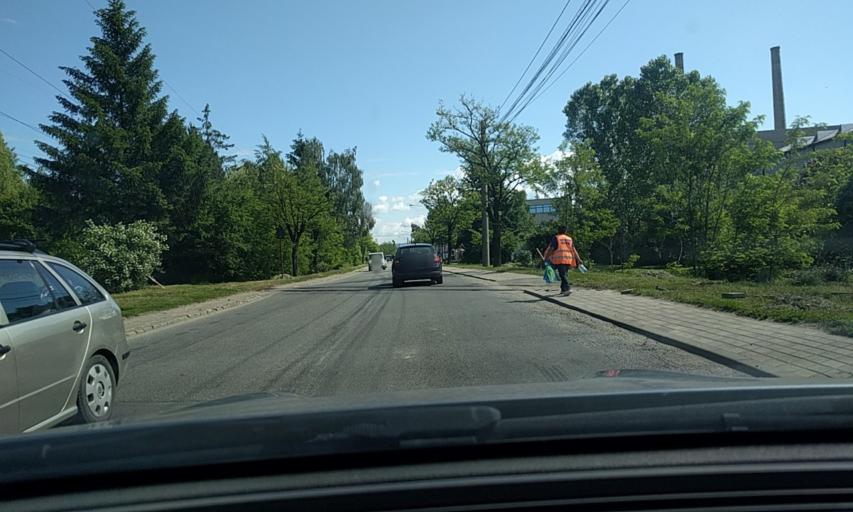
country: RO
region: Bistrita-Nasaud
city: Bistrita
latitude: 47.1341
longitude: 24.4748
